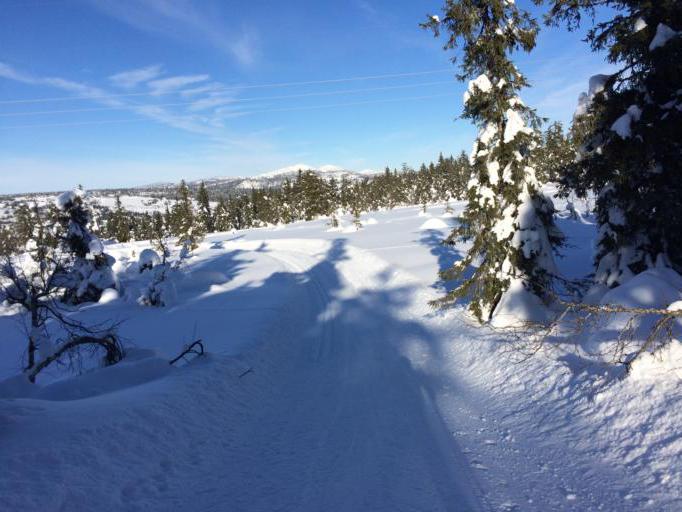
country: NO
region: Oppland
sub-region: Gausdal
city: Segalstad bru
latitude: 61.3131
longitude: 10.1058
